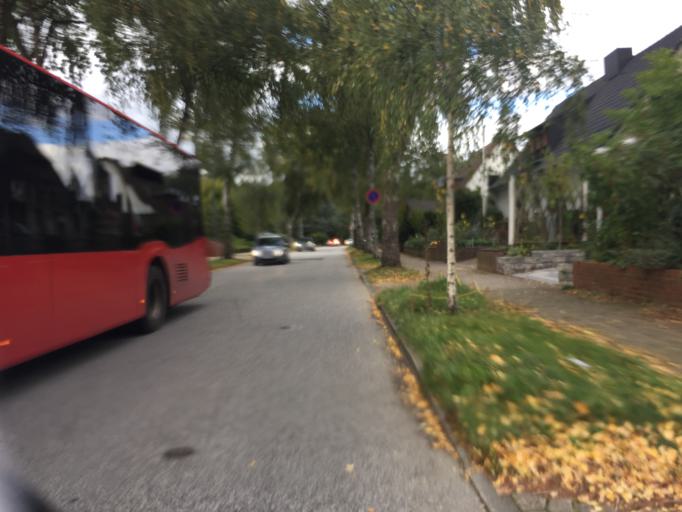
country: DE
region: Schleswig-Holstein
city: Itzehoe
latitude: 53.9424
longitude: 9.5090
